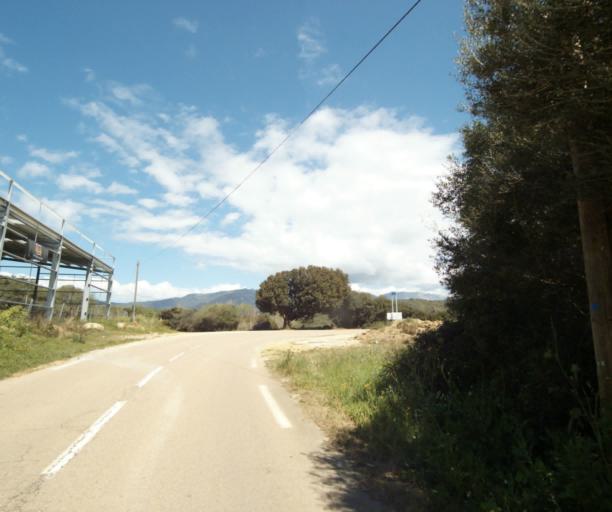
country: FR
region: Corsica
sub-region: Departement de la Corse-du-Sud
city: Propriano
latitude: 41.6573
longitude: 8.8938
